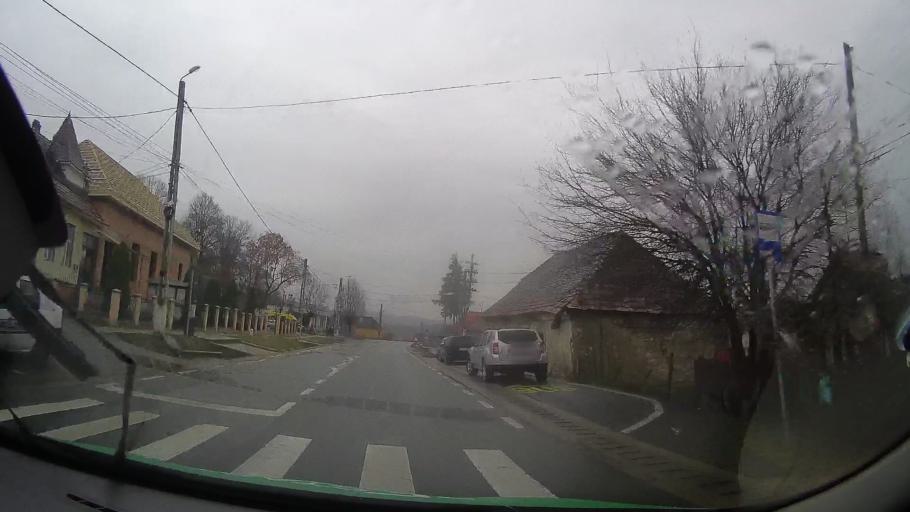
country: RO
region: Bistrita-Nasaud
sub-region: Comuna Galatii Bistritei
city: Galatii Bistritei
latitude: 46.9921
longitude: 24.4213
